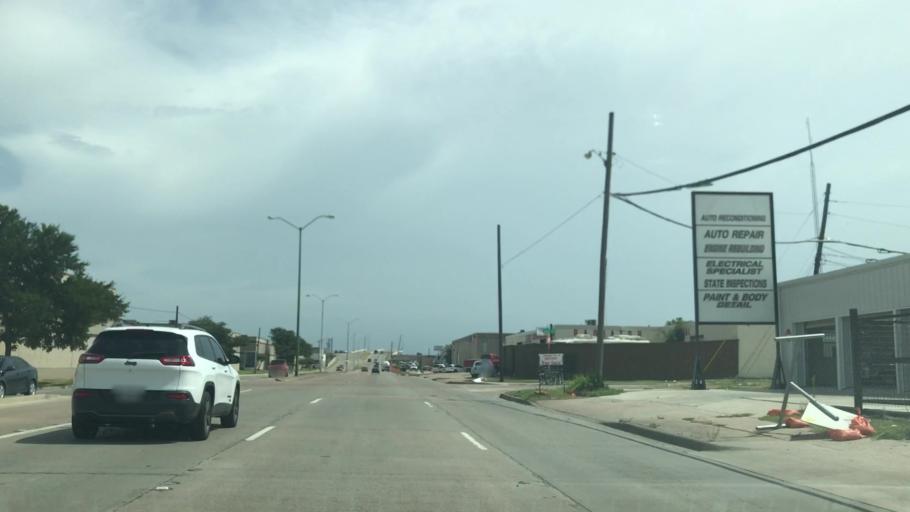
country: US
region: Texas
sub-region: Dallas County
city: Dallas
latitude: 32.8071
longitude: -96.8738
